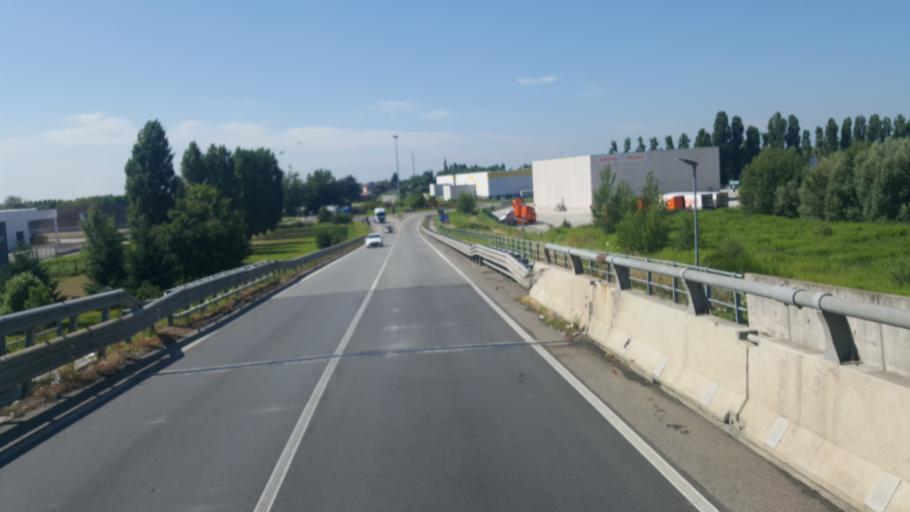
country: IT
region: Piedmont
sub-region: Provincia di Novara
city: Vicolungo
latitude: 45.4655
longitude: 8.4645
